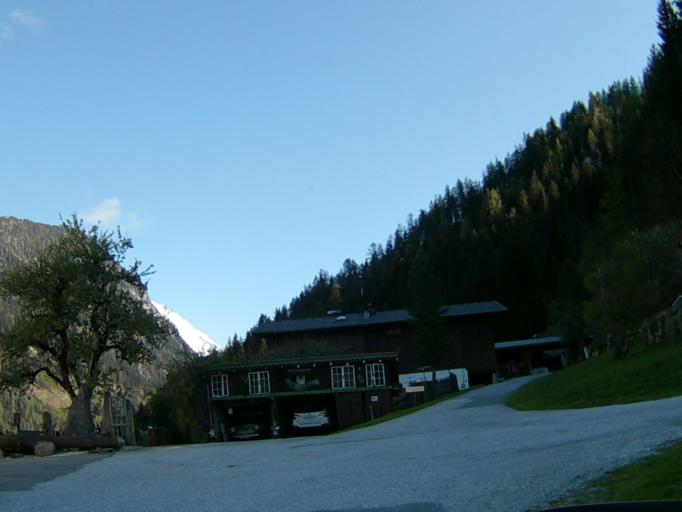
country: AT
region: Salzburg
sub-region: Politischer Bezirk Zell am See
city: Wald im Pinzgau
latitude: 47.2389
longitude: 12.2414
